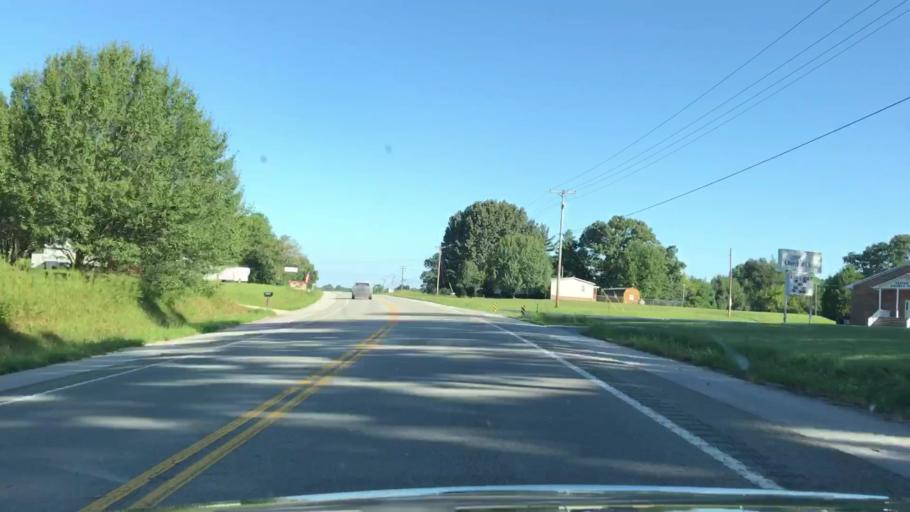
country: US
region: Tennessee
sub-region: Jackson County
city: Dodson Branch
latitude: 36.2628
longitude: -85.6112
